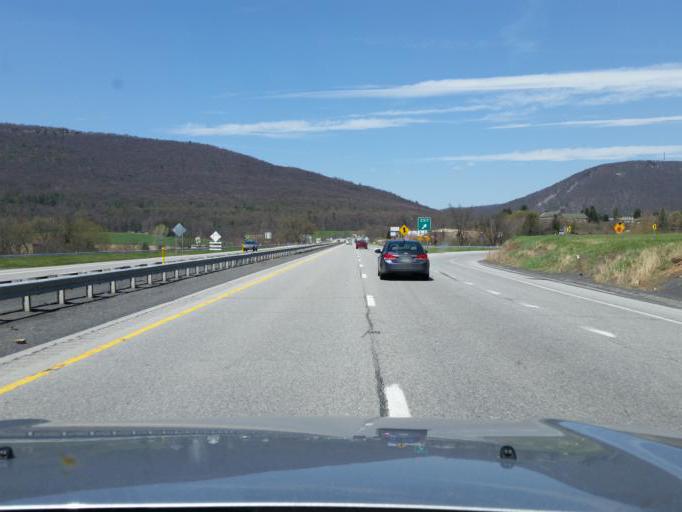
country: US
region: Pennsylvania
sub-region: Mifflin County
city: Yeagertown
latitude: 40.6292
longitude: -77.5829
